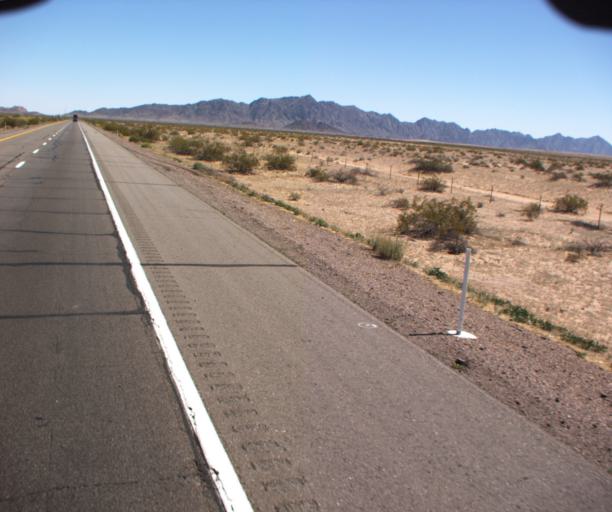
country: US
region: Arizona
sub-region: Yuma County
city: Wellton
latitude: 32.7130
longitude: -113.8240
